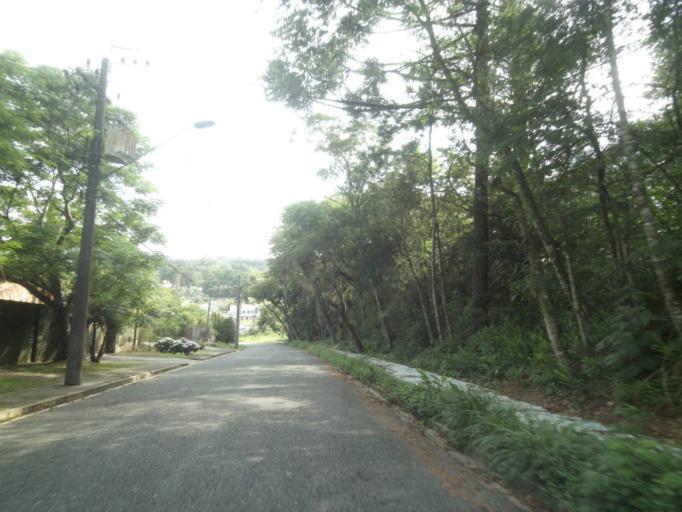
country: BR
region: Parana
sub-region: Curitiba
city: Curitiba
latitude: -25.4116
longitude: -49.3155
